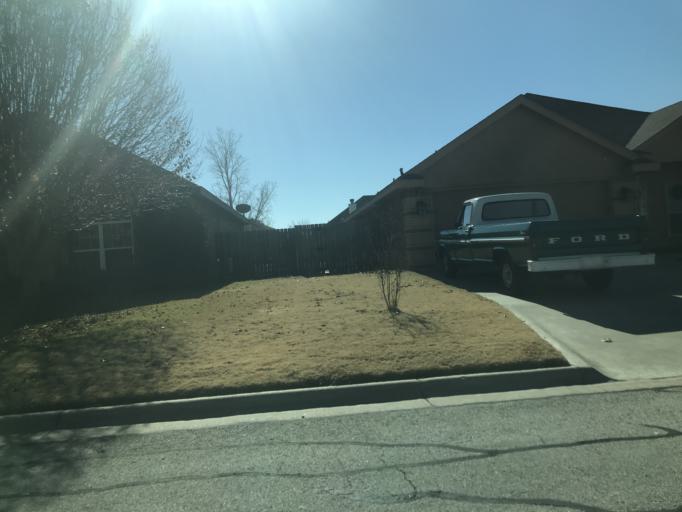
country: US
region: Texas
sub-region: Taylor County
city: Abilene
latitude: 32.4917
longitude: -99.6883
